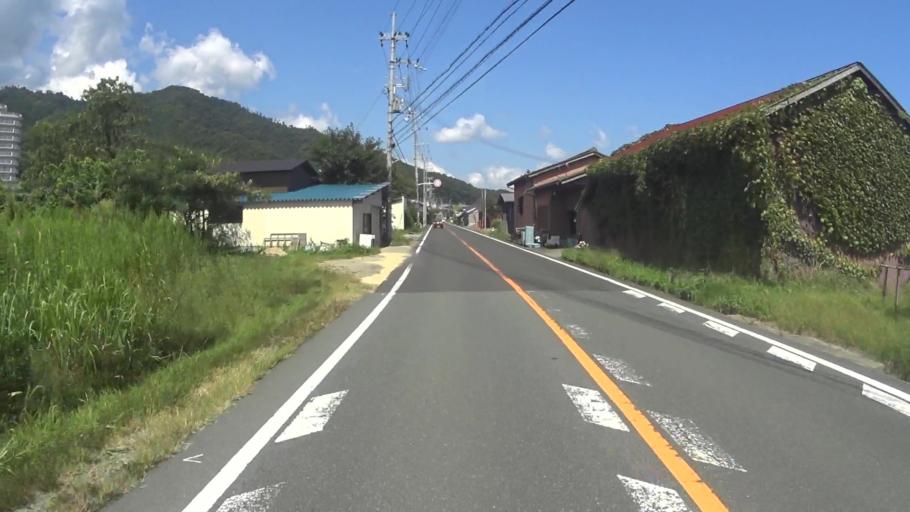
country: JP
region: Kyoto
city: Miyazu
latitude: 35.5857
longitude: 135.2061
